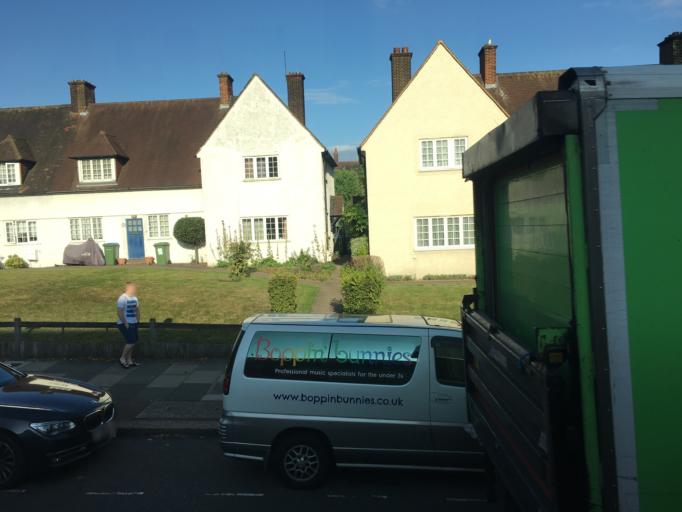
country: GB
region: England
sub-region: Greater London
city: Woolwich
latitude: 51.4595
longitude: 0.0498
